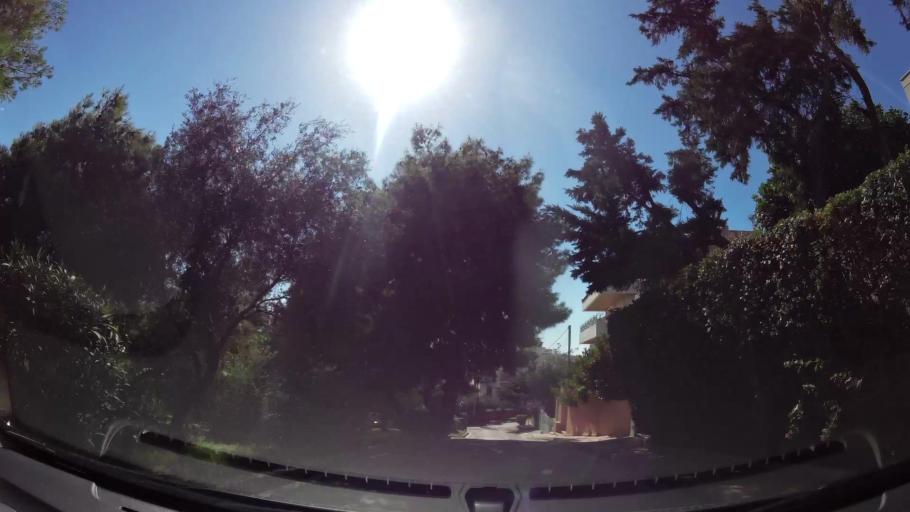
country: GR
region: Attica
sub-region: Nomarchia Anatolikis Attikis
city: Voula
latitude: 37.8443
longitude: 23.7752
